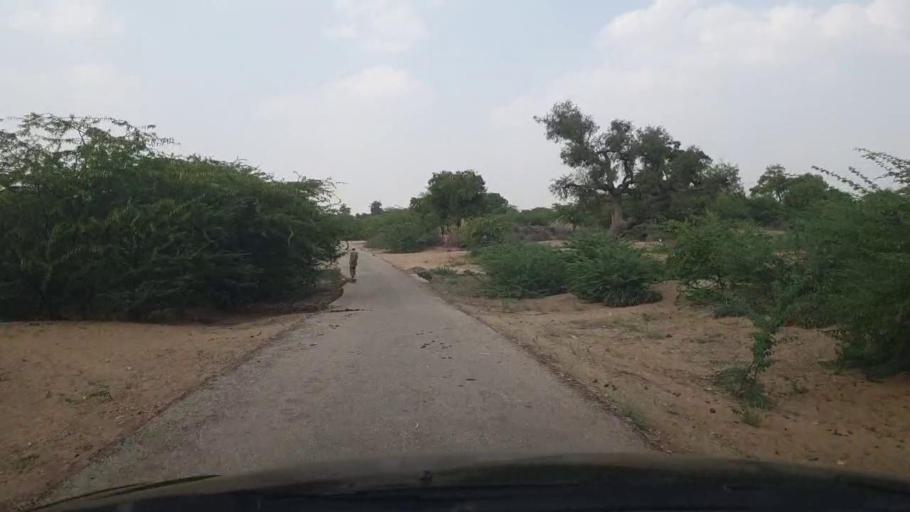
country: PK
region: Sindh
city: Islamkot
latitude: 24.9899
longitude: 70.5775
